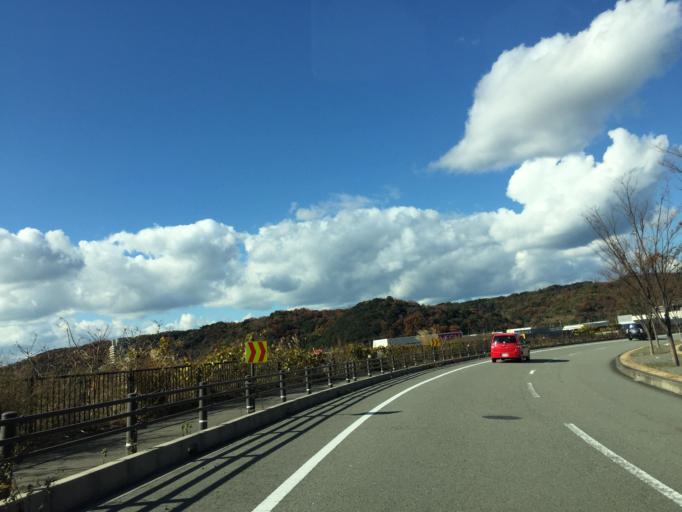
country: JP
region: Wakayama
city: Wakayama-shi
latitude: 34.2734
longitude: 135.1514
